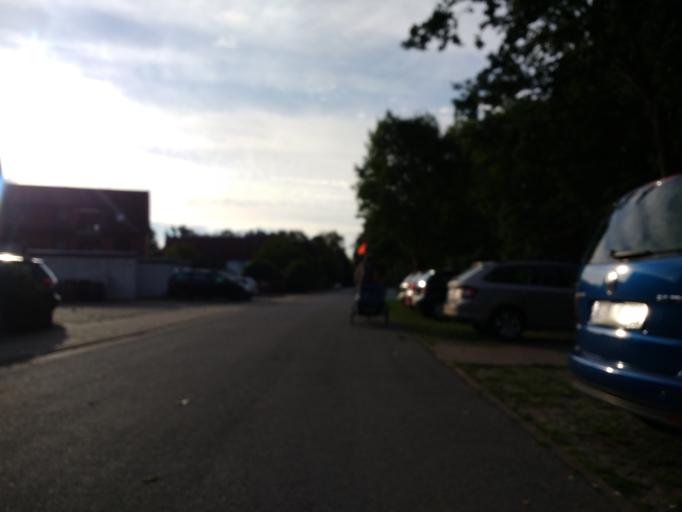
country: DE
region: Lower Saxony
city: Isenbuttel
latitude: 52.4389
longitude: 10.5693
